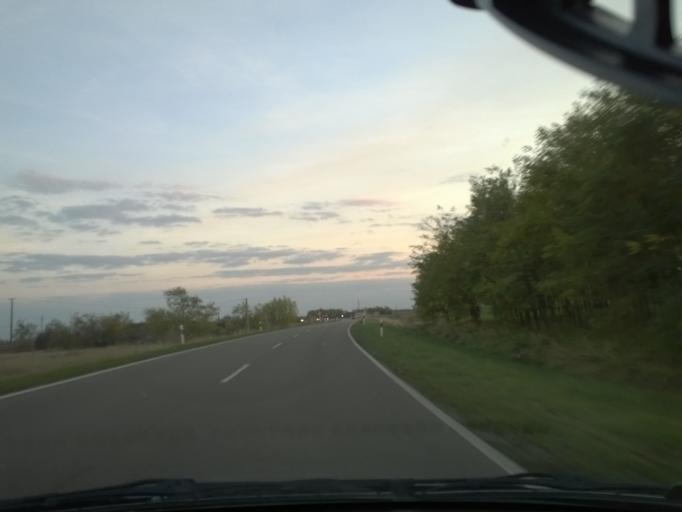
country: HU
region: Csongrad
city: Csongrad
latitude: 46.7134
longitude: 20.1143
